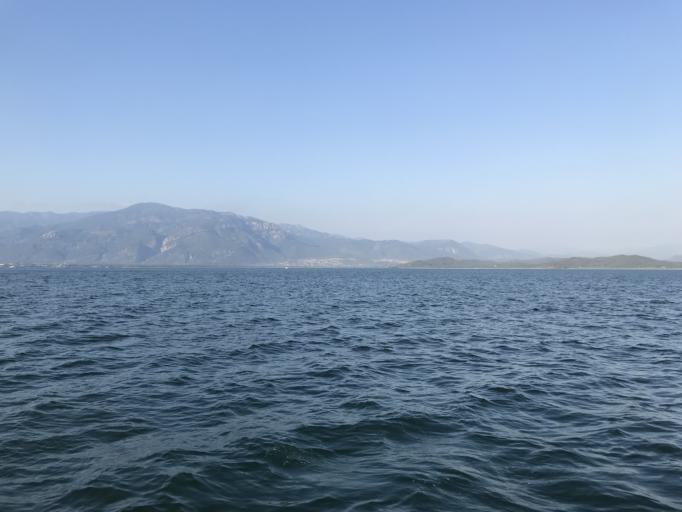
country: TR
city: Dalyan
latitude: 36.9181
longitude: 28.6488
